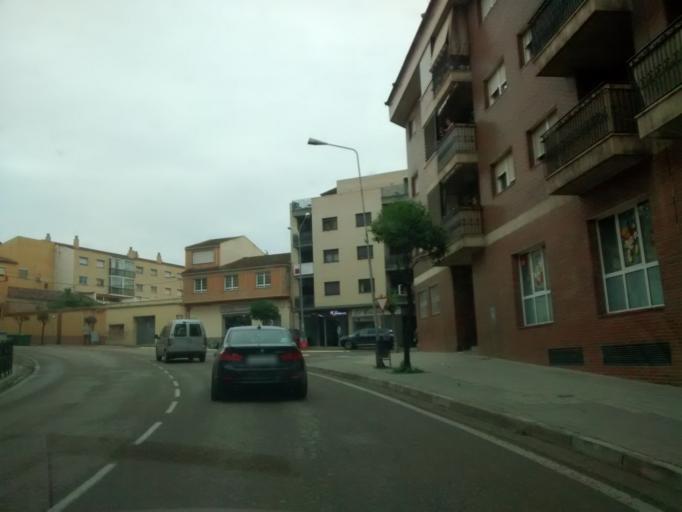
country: ES
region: Aragon
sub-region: Provincia de Zaragoza
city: Caspe
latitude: 41.2343
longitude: -0.0444
